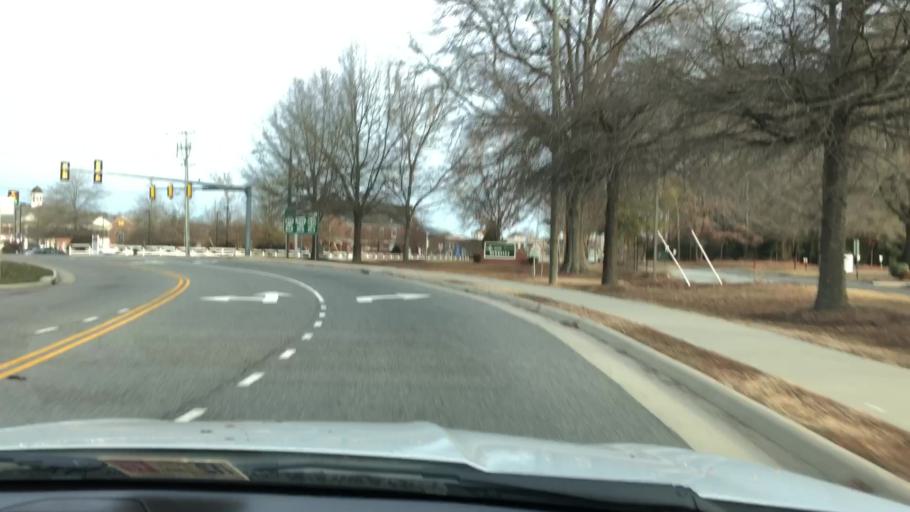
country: US
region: Virginia
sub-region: James City County
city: Williamsburg
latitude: 37.2736
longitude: -76.7388
